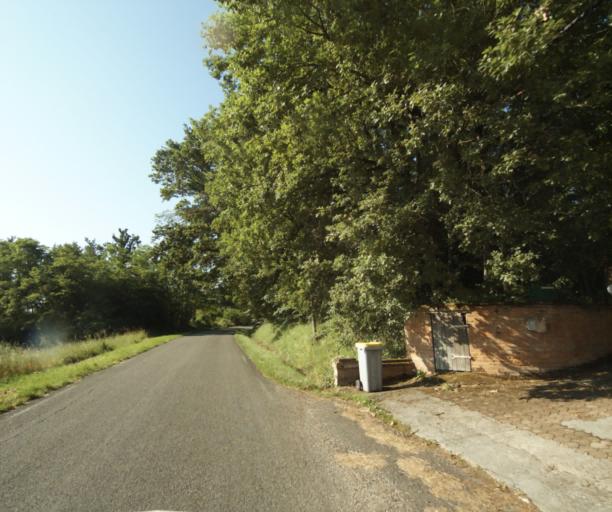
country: FR
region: Midi-Pyrenees
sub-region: Departement du Tarn-et-Garonne
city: Saint-Etienne-de-Tulmont
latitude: 44.0196
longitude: 1.4301
